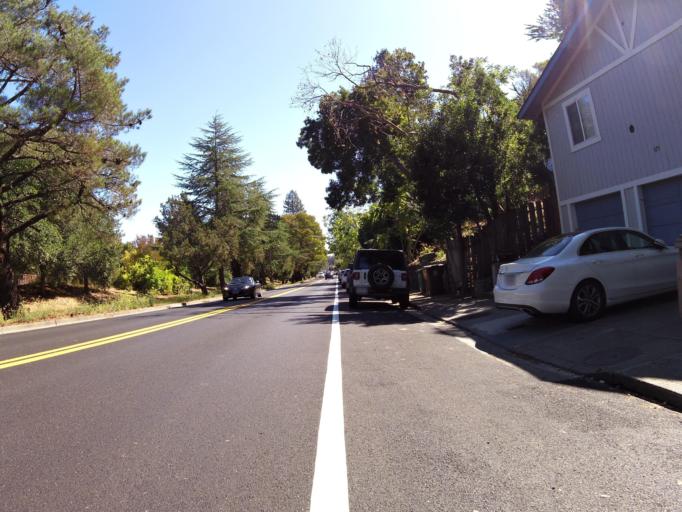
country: US
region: California
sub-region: Marin County
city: Larkspur
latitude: 37.9405
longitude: -122.5375
